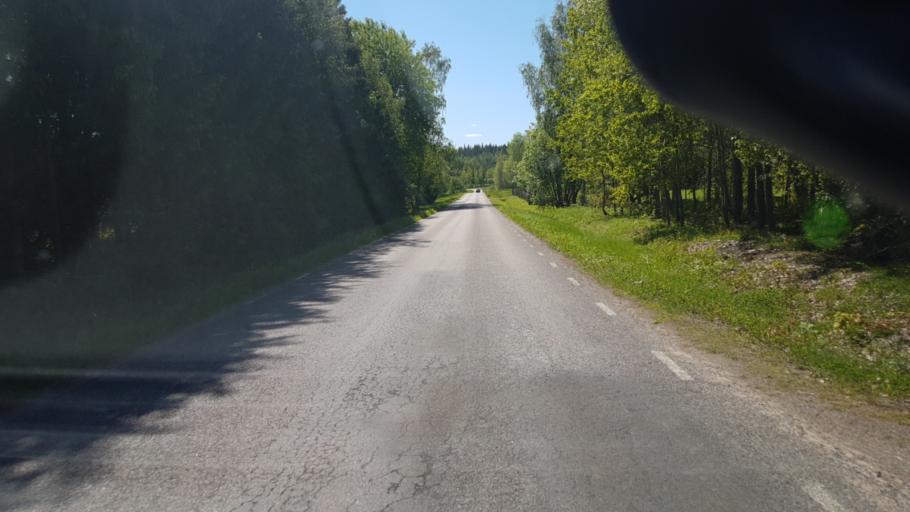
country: SE
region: Vaermland
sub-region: Grums Kommun
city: Slottsbron
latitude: 59.4657
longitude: 12.8758
